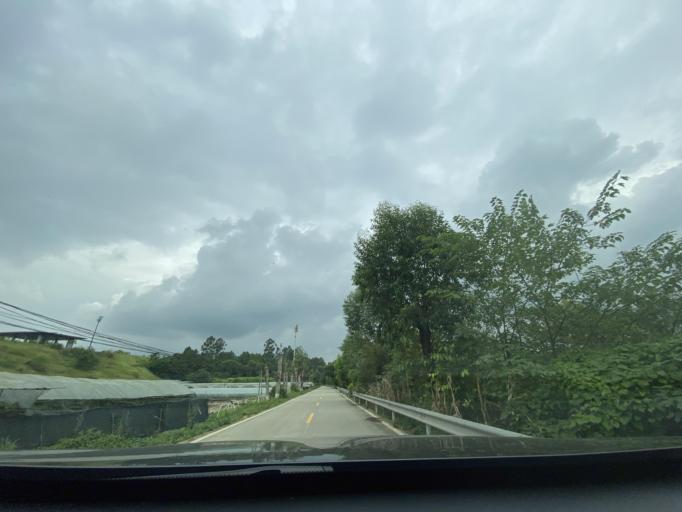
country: CN
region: Sichuan
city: Wujin
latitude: 30.3908
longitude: 103.9670
